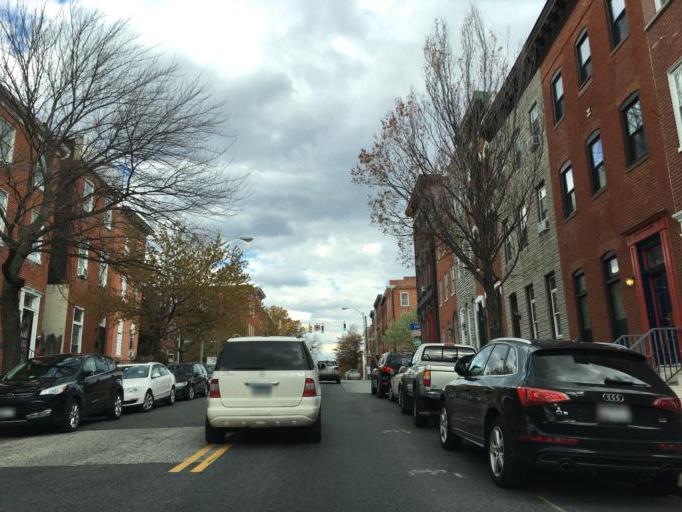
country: US
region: Maryland
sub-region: City of Baltimore
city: Baltimore
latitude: 39.2894
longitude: -76.5898
